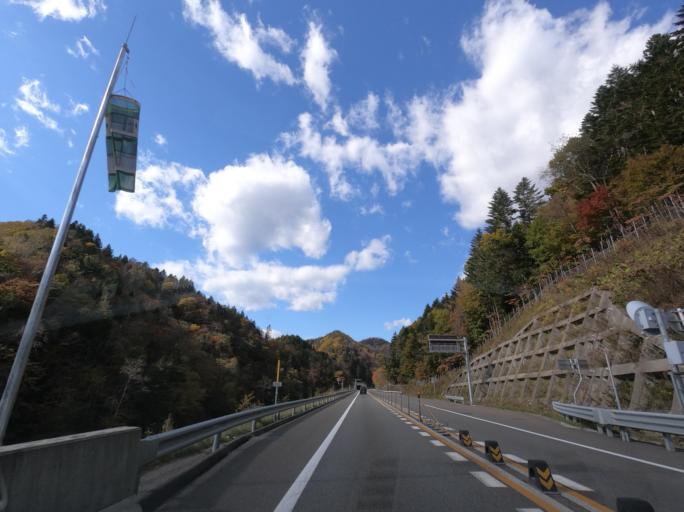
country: JP
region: Hokkaido
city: Kushiro
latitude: 43.0803
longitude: 144.0285
